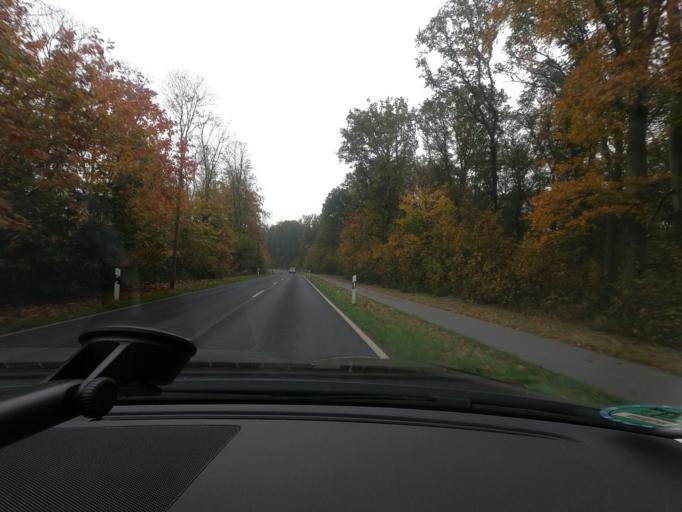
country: DE
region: North Rhine-Westphalia
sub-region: Regierungsbezirk Dusseldorf
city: Kevelaer
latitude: 51.5897
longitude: 6.2982
